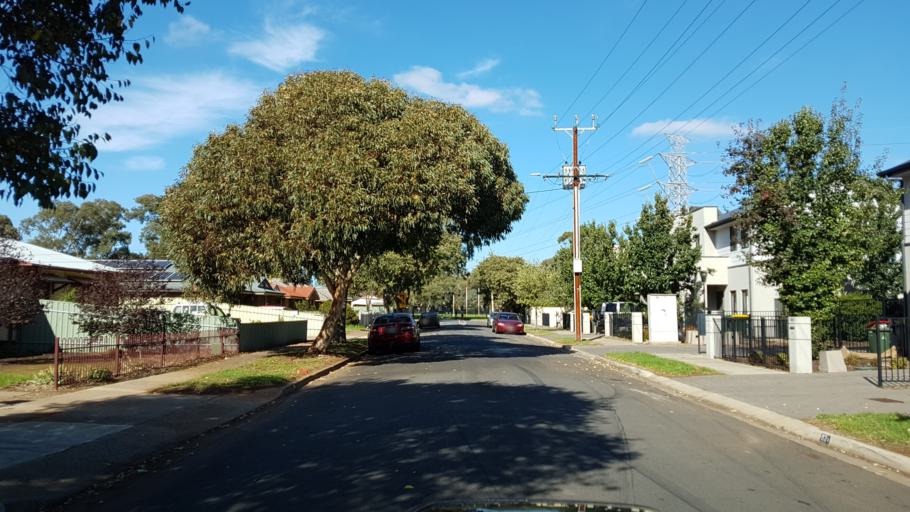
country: AU
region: South Australia
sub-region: Salisbury
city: Salisbury
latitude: -34.7558
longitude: 138.6377
